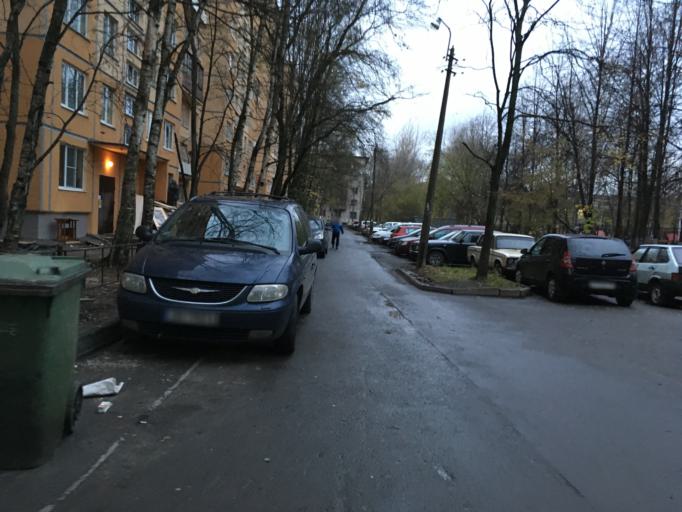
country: RU
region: St.-Petersburg
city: Obukhovo
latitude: 59.9048
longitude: 30.4714
